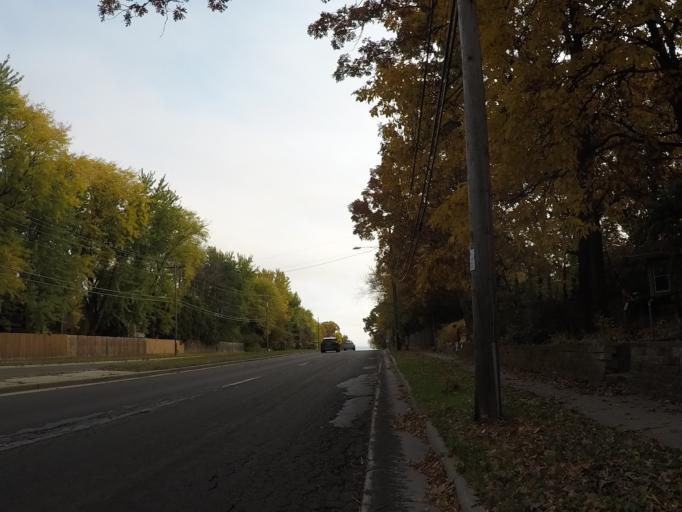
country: US
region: Wisconsin
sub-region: Dane County
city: Middleton
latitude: 43.1081
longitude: -89.4792
